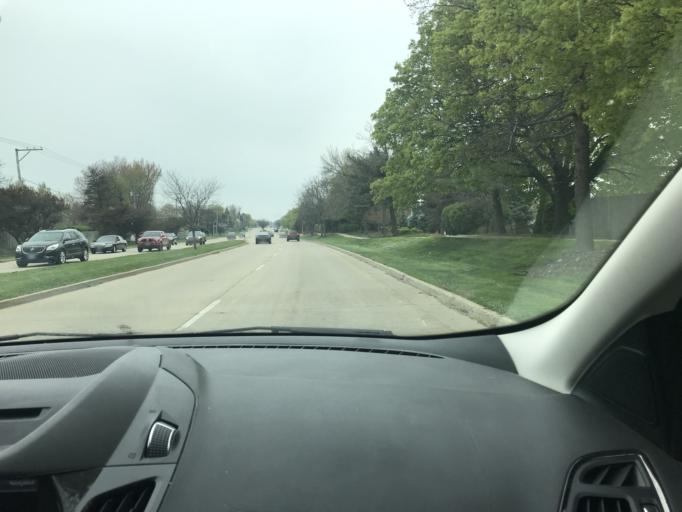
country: US
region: Illinois
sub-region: Kane County
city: Aurora
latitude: 41.7368
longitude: -88.2553
